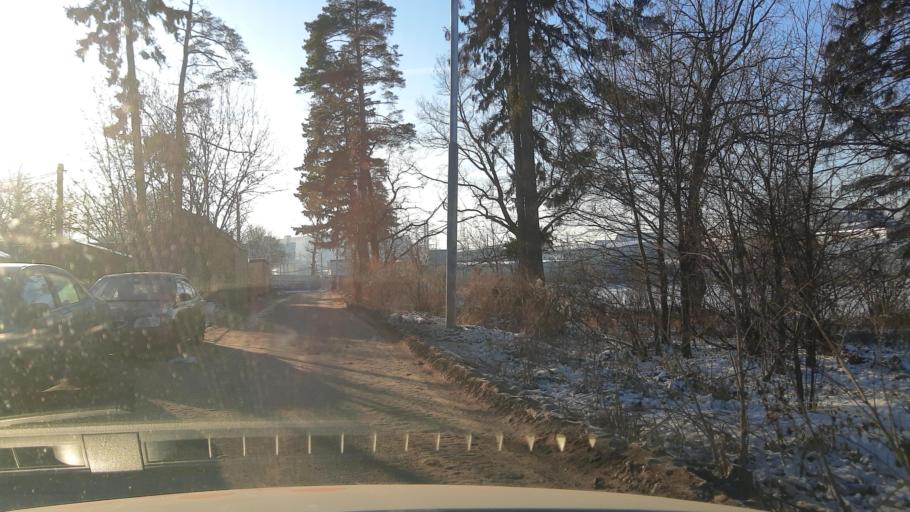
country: RU
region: Moskovskaya
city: Mosrentgen
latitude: 55.6062
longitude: 37.4683
